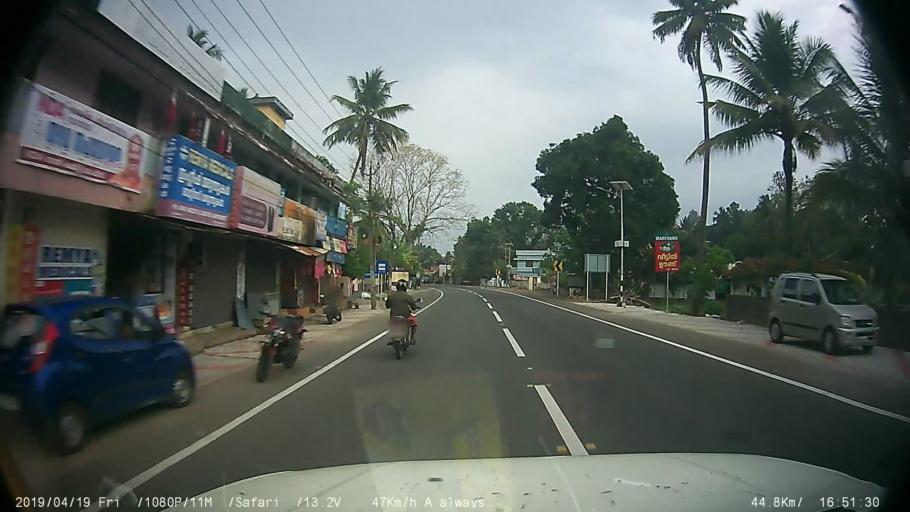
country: IN
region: Kerala
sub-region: Kottayam
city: Changanacheri
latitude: 9.4568
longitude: 76.5337
